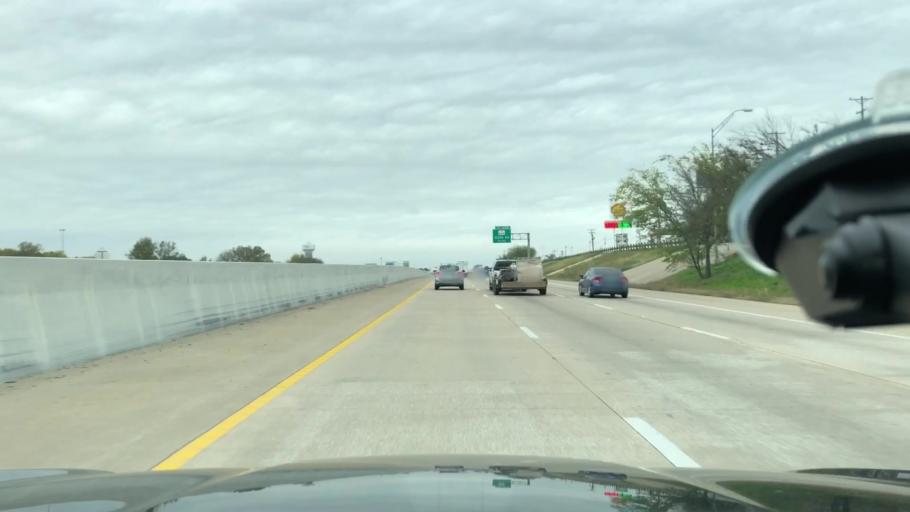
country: US
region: Texas
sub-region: Ellis County
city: Red Oak
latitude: 32.5139
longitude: -96.8221
